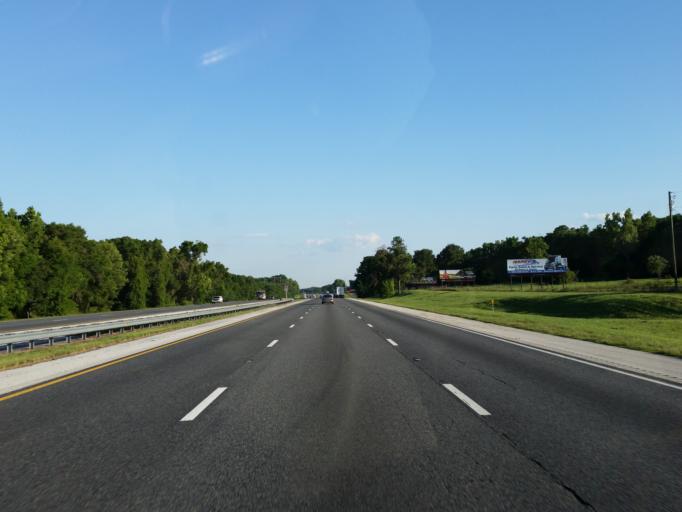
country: US
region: Florida
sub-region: Marion County
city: Citra
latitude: 29.3130
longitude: -82.2093
